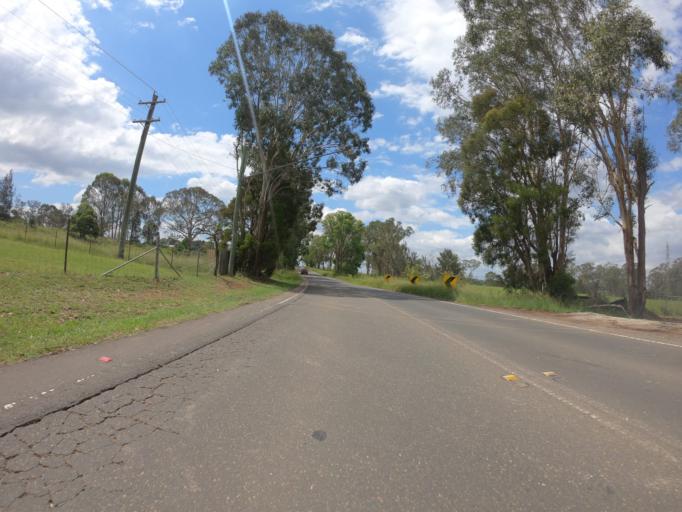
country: AU
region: New South Wales
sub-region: Penrith Municipality
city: Kingswood Park
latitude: -33.8280
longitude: 150.7591
